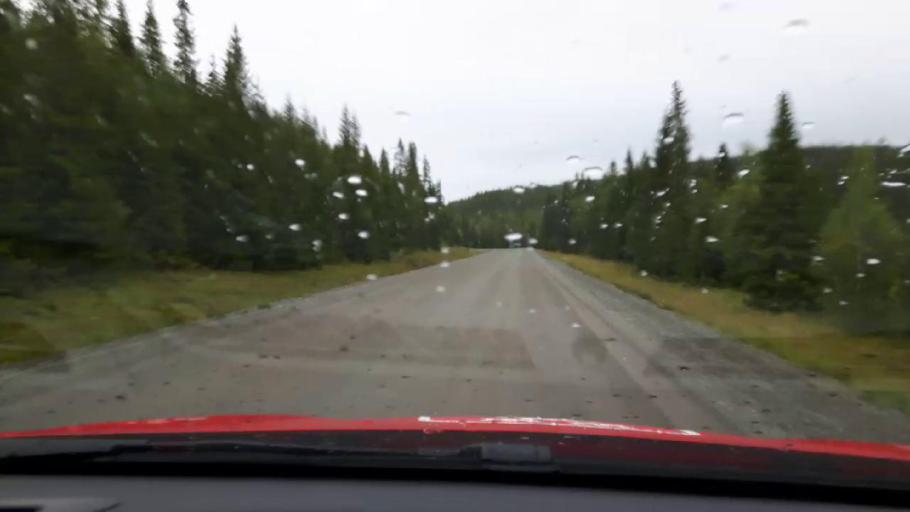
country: SE
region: Jaemtland
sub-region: Are Kommun
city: Are
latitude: 63.4249
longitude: 12.7408
